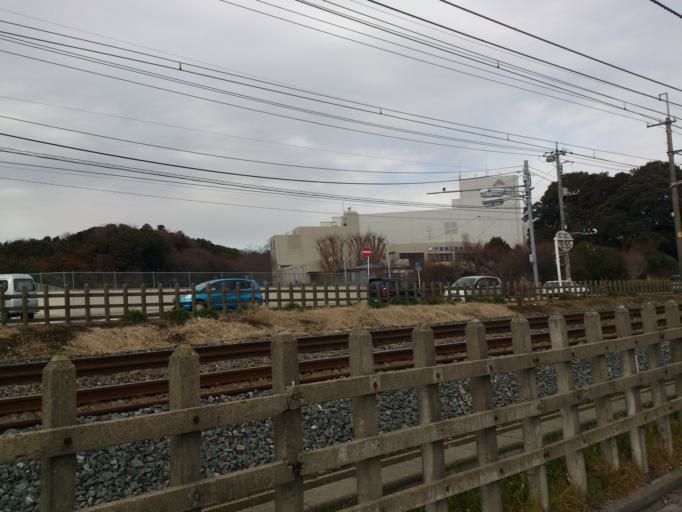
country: JP
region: Chiba
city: Matsudo
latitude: 35.7973
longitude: 139.9410
